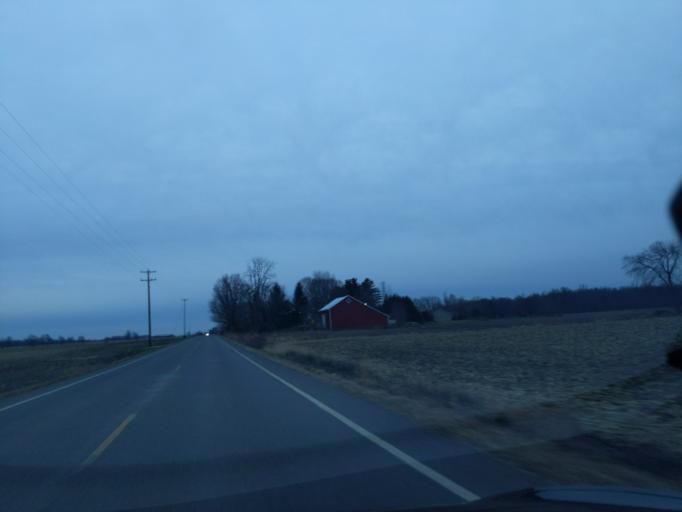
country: US
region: Michigan
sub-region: Ionia County
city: Portland
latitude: 42.8976
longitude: -84.9561
